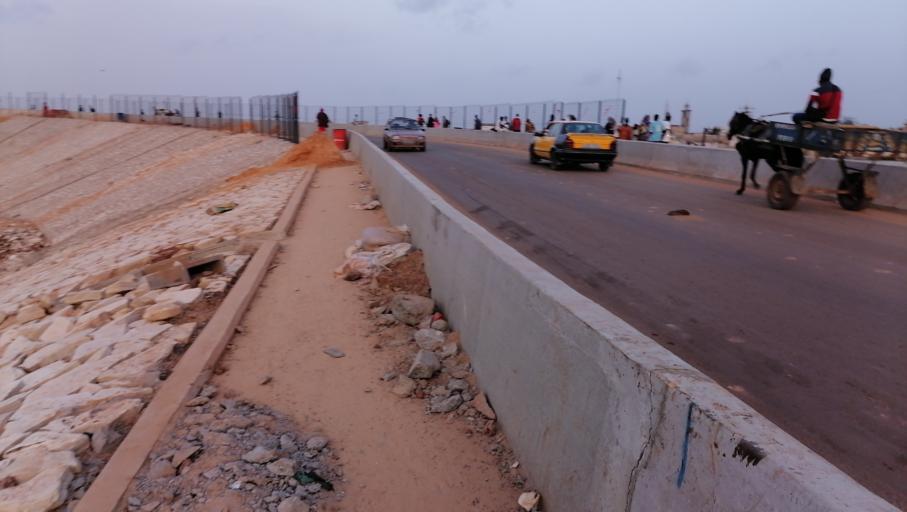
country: SN
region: Dakar
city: Pikine
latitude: 14.7592
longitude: -17.3806
